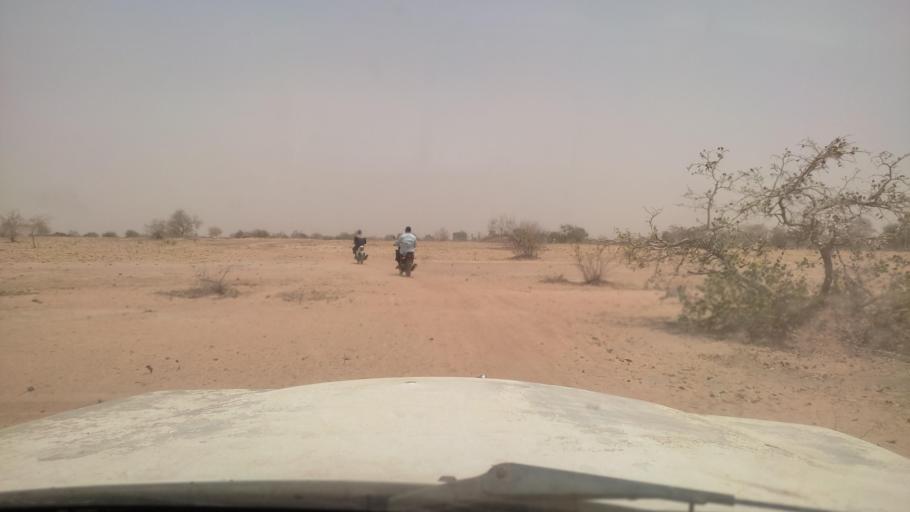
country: BF
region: Est
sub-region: Gnagna Province
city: Bogande
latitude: 13.0012
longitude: -0.0960
